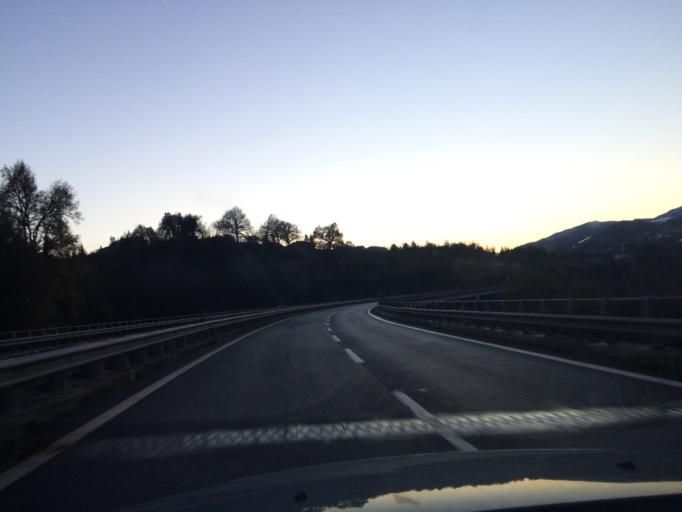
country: IT
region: Emilia-Romagna
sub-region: Forli-Cesena
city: Sarsina
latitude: 43.9253
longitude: 12.1713
